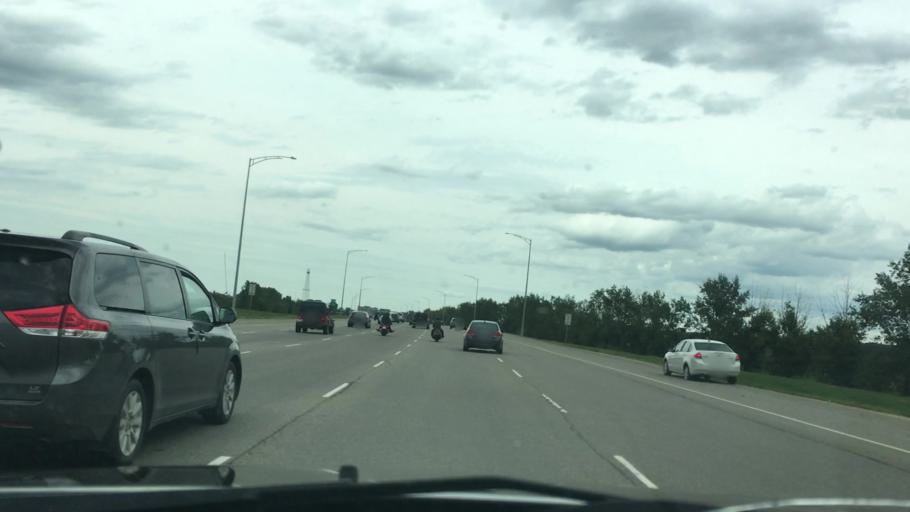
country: CA
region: Alberta
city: Beaumont
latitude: 53.4033
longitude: -113.5027
